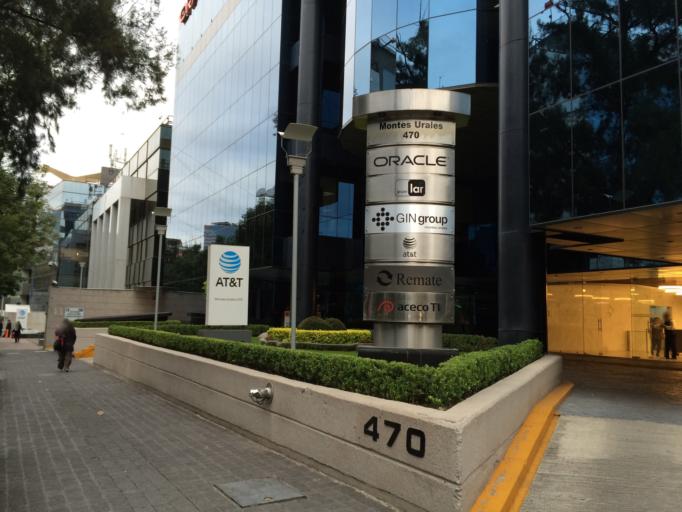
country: MX
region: Mexico City
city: Miguel Hidalgo
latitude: 19.4283
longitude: -99.2058
